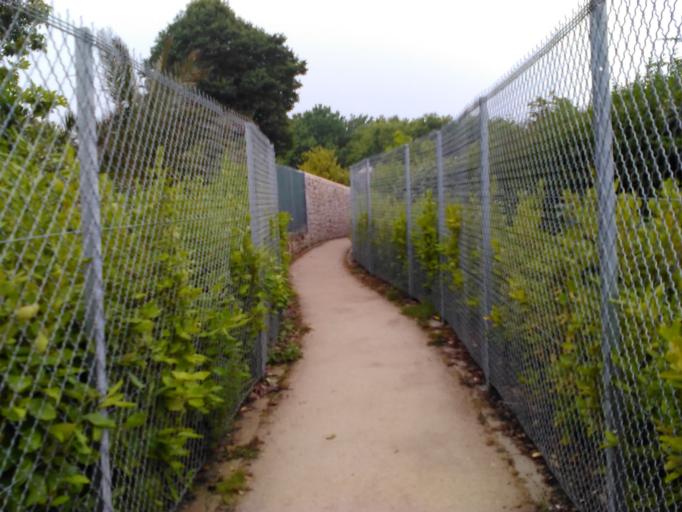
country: FR
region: Brittany
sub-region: Departement du Finistere
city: Fouesnant
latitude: 47.8559
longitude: -3.9767
